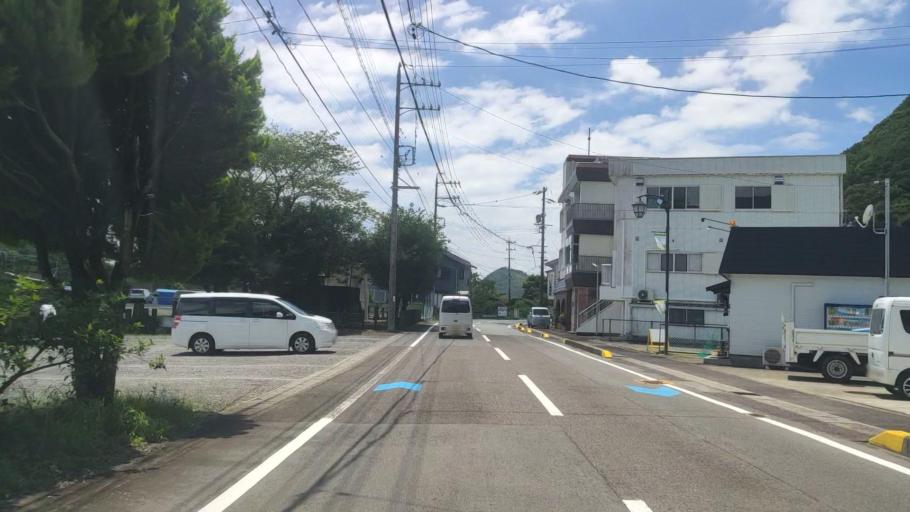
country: JP
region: Mie
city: Owase
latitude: 34.2096
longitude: 136.3484
